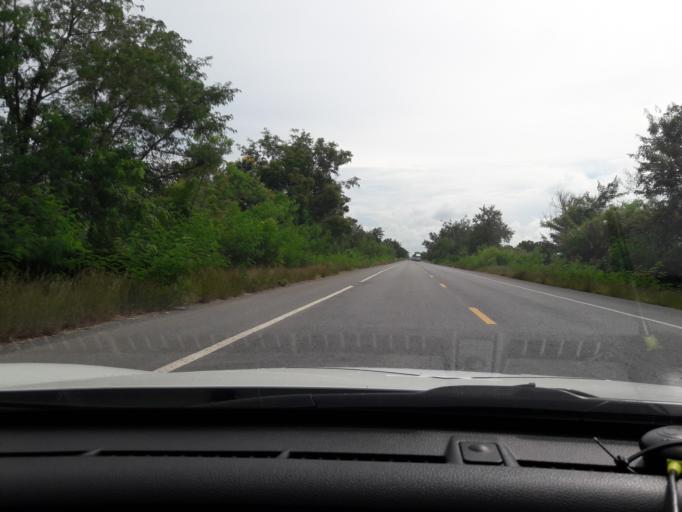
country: TH
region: Nakhon Sawan
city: Phai Sali
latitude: 15.5326
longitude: 100.5500
